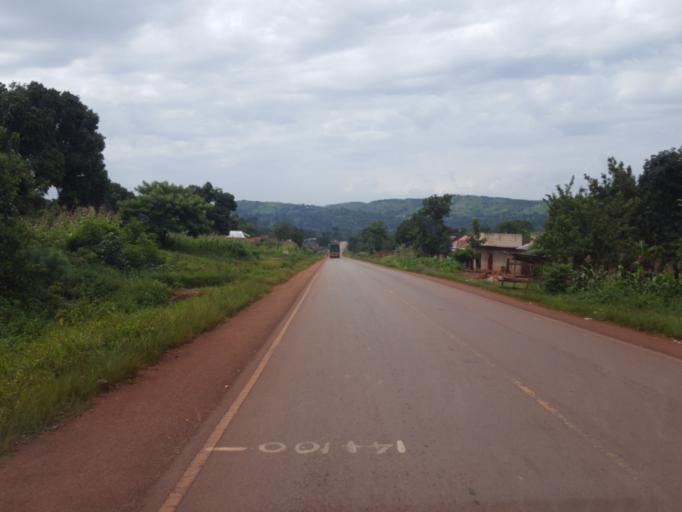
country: UG
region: Central Region
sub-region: Mityana District
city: Mityana
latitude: 0.6363
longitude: 32.1067
